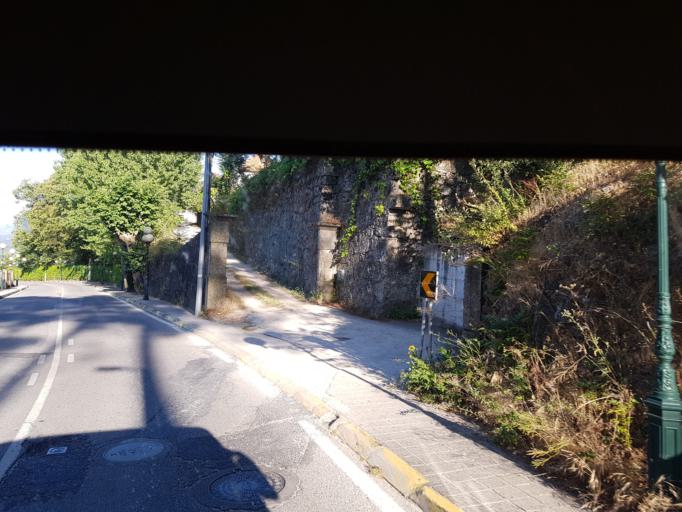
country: PT
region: Castelo Branco
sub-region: Covilha
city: Covilha
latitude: 40.2762
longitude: -7.5085
